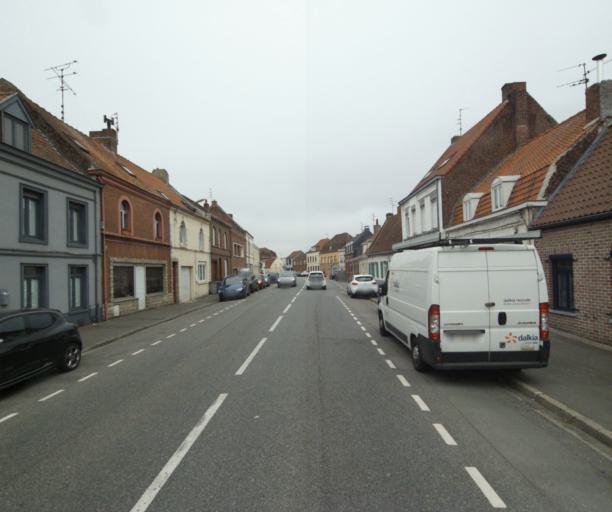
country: FR
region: Nord-Pas-de-Calais
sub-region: Departement du Nord
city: Baisieux
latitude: 50.6086
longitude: 3.2526
